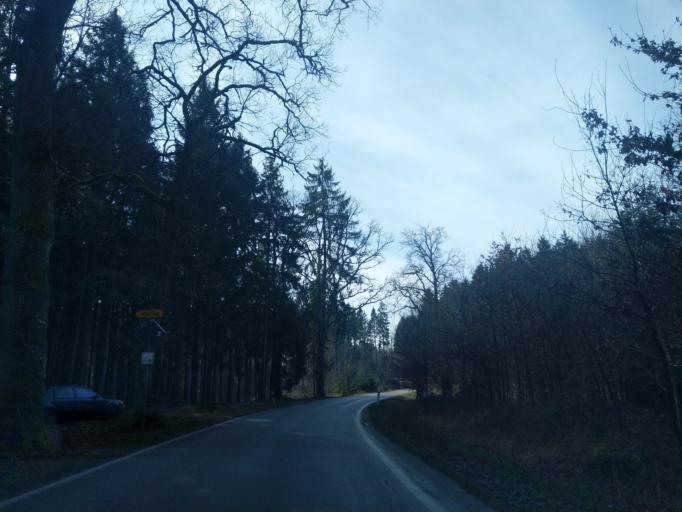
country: DE
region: Bavaria
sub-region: Lower Bavaria
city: Buchhofen
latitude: 48.6593
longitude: 12.9157
